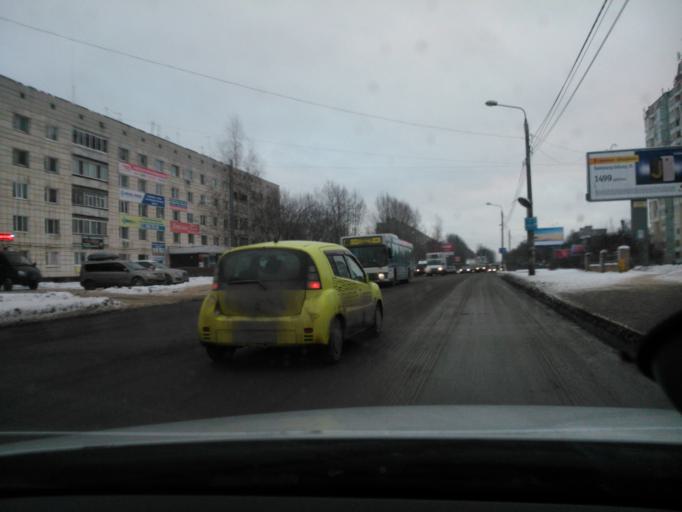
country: RU
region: Perm
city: Kondratovo
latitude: 57.9677
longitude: 56.1745
